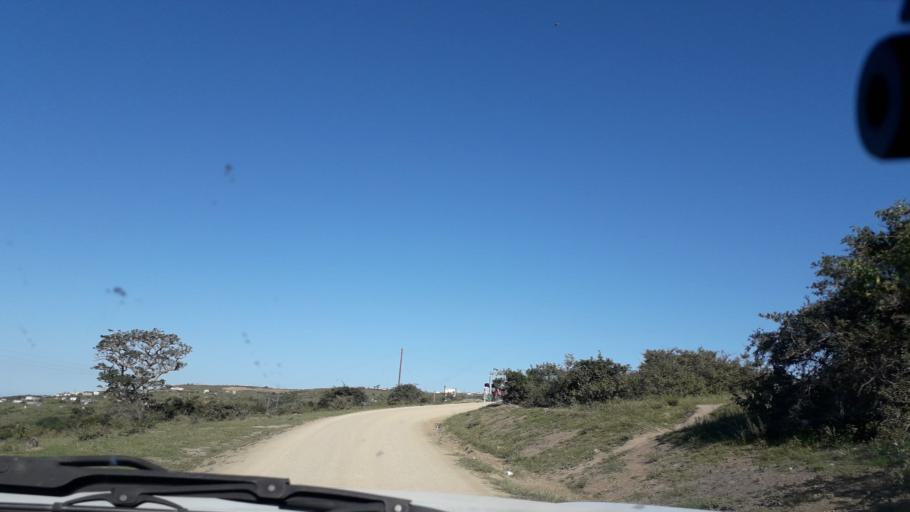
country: ZA
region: Eastern Cape
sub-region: Buffalo City Metropolitan Municipality
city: East London
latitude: -32.7994
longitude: 27.9667
